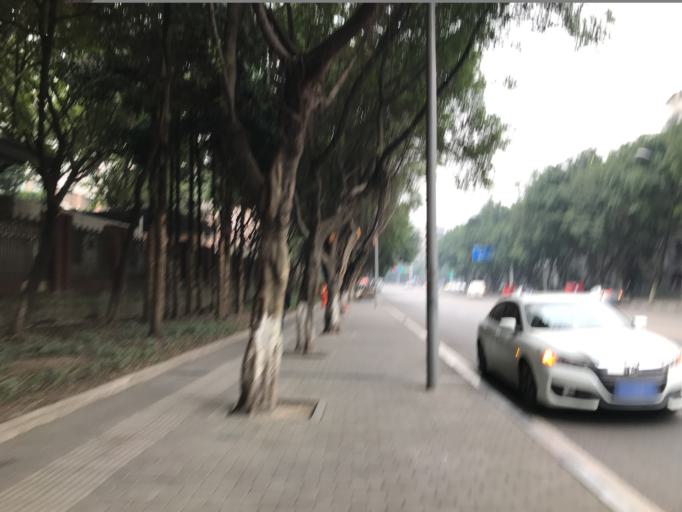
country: CN
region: Chongqing Shi
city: Chongqing
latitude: 29.5273
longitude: 106.5492
